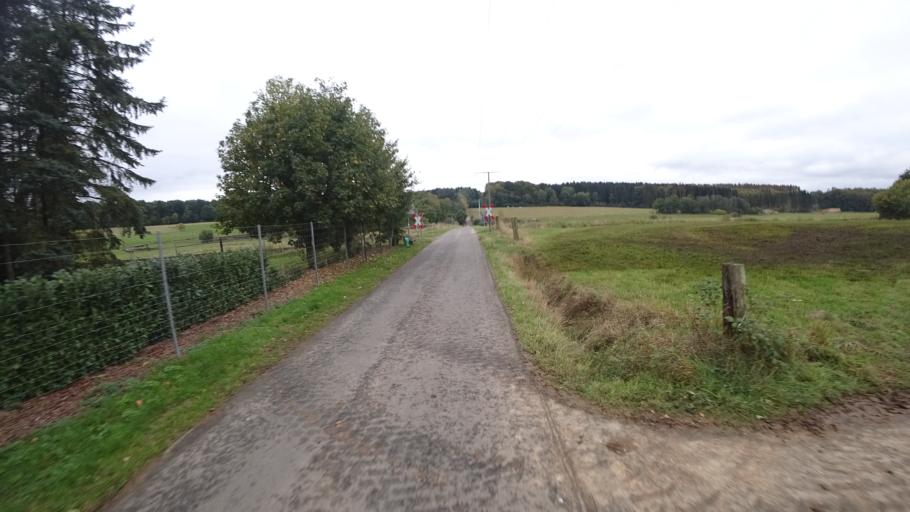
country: DE
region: Rheinland-Pfalz
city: Marienrachdorf
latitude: 50.5460
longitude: 7.7101
